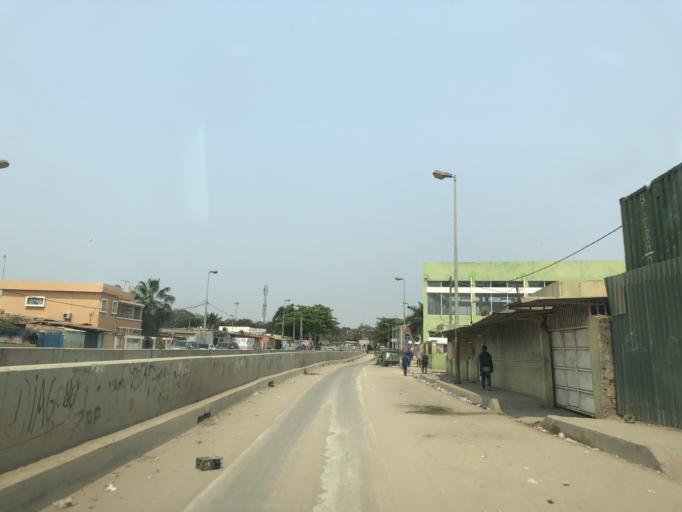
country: AO
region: Luanda
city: Luanda
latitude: -8.8489
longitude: 13.2078
